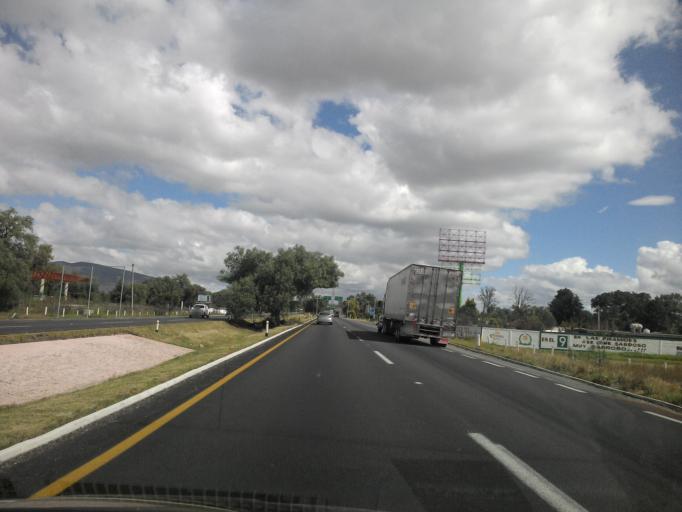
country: MX
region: Morelos
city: Xometla
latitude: 19.6498
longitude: -98.8863
